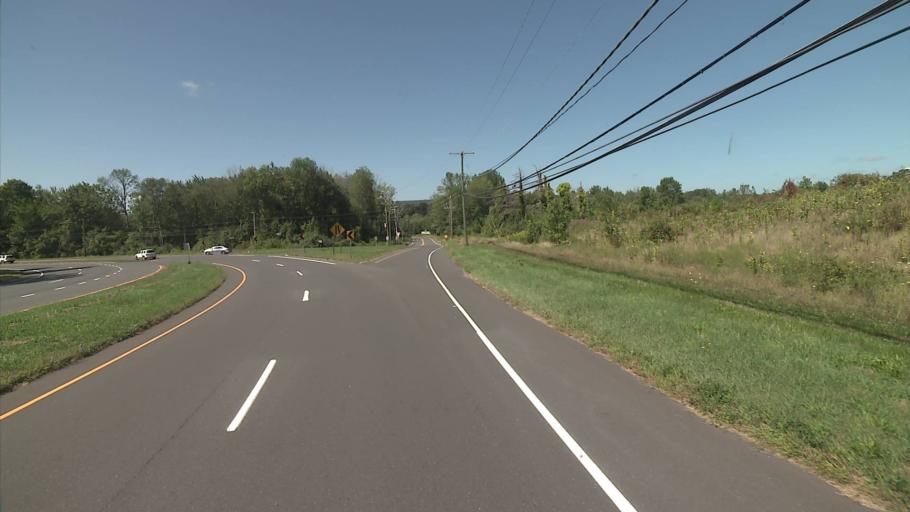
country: US
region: Connecticut
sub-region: Hartford County
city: Blue Hills
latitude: 41.8169
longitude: -72.7469
